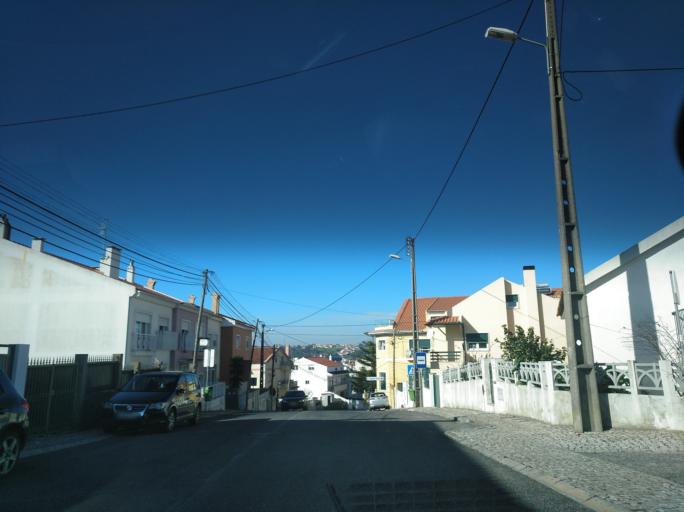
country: PT
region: Lisbon
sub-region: Odivelas
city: Canecas
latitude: 38.8044
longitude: -9.2189
